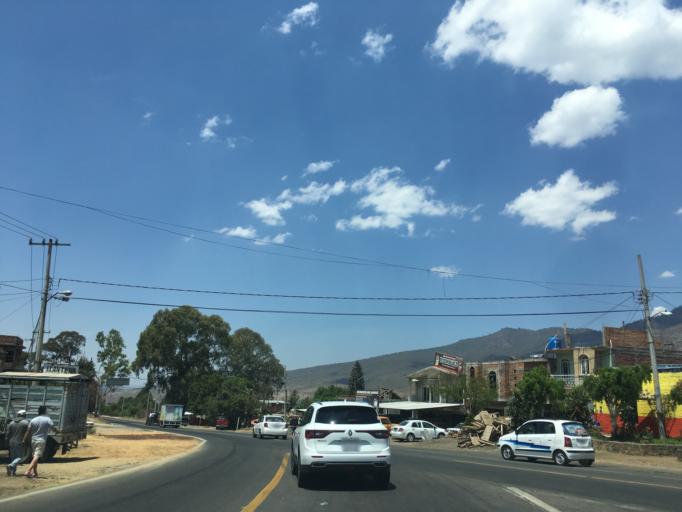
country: MX
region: Michoacan
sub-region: Chilchota
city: Tacuro (Santa Maria Tacuro)
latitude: 19.8519
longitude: -102.0330
